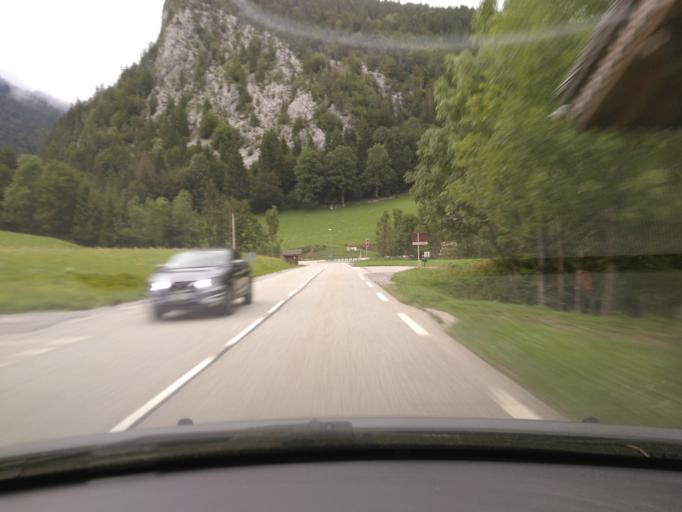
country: FR
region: Rhone-Alpes
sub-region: Departement de la Haute-Savoie
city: Saint-Jean-de-Sixt
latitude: 45.9302
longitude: 6.4052
